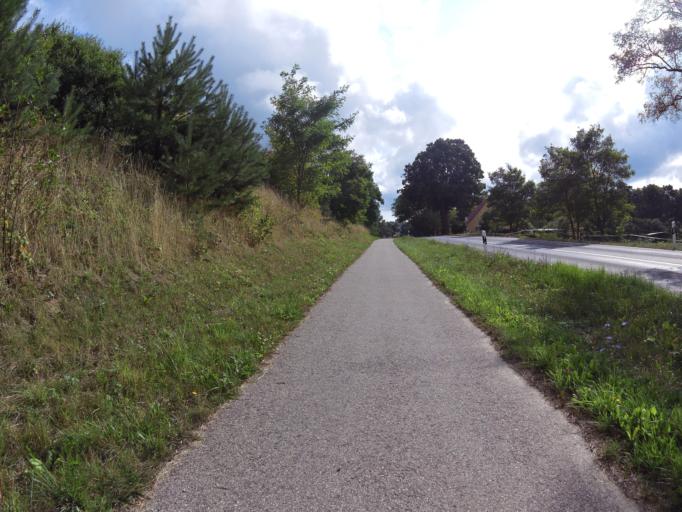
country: DE
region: Mecklenburg-Vorpommern
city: Seebad Bansin
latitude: 53.9624
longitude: 14.0626
